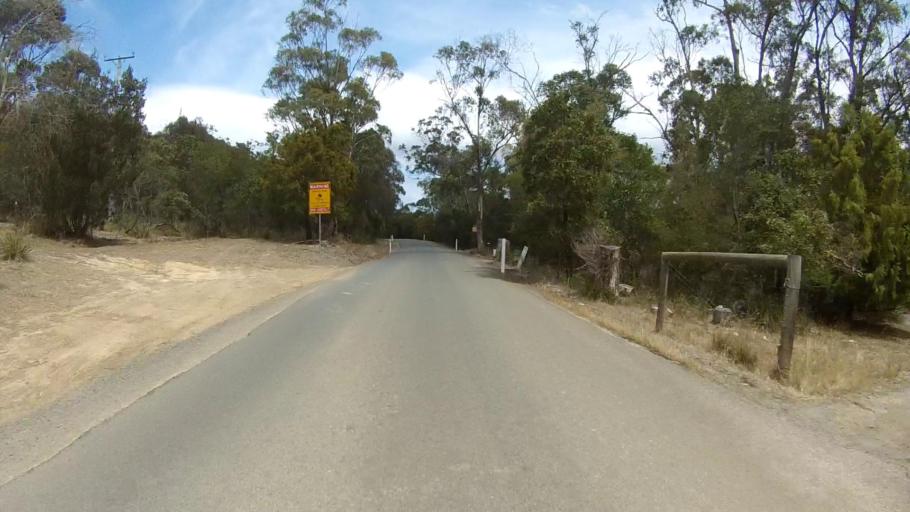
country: AU
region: Tasmania
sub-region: Kingborough
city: Blackmans Bay
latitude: -43.0353
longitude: 147.3059
